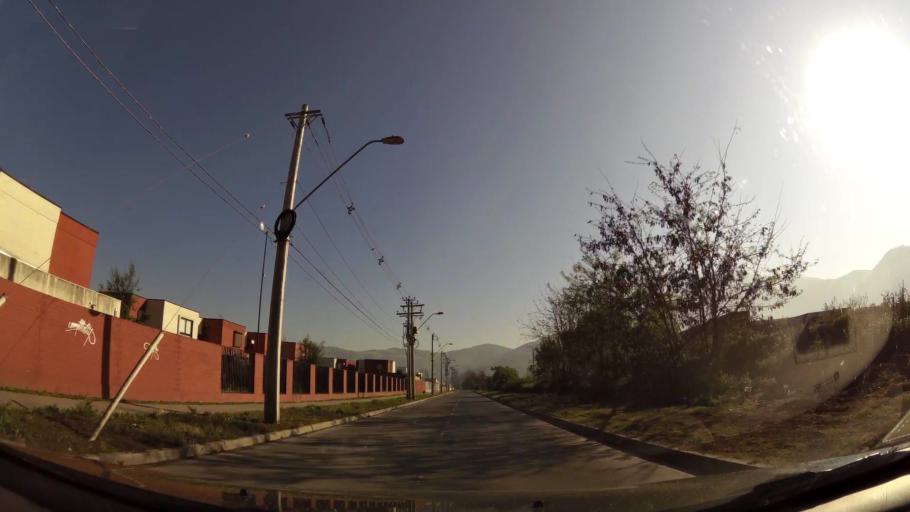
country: CL
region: Santiago Metropolitan
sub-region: Provincia de Chacabuco
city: Chicureo Abajo
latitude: -33.3675
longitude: -70.6652
